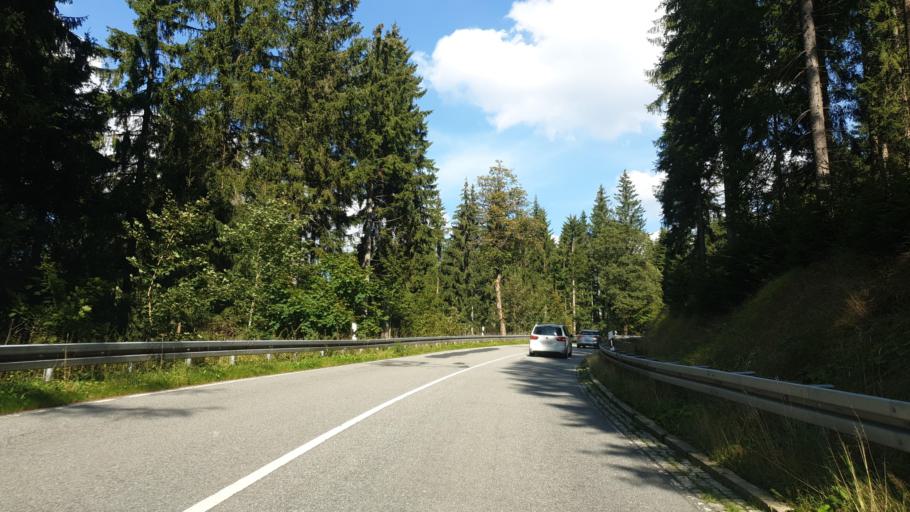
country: DE
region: Saxony
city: Johanngeorgenstadt
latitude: 50.4347
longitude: 12.6501
